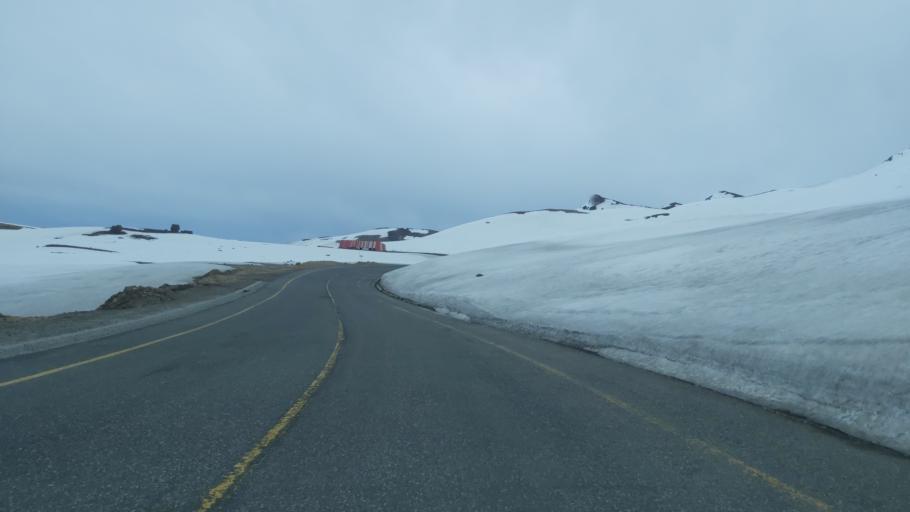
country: CL
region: Maule
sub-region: Provincia de Linares
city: Colbun
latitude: -36.0064
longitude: -70.4739
